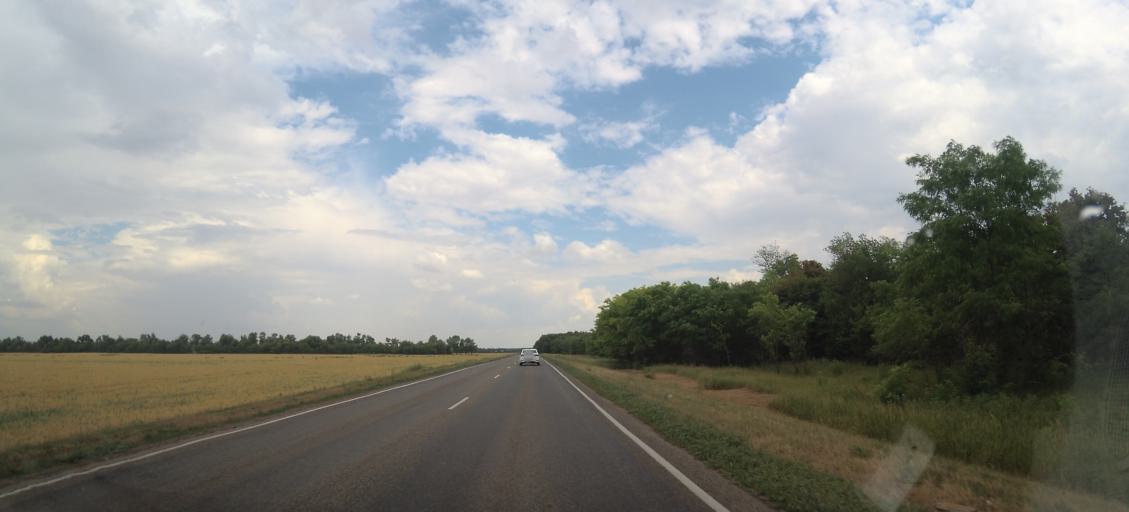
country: RU
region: Rostov
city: Peschanokopskoye
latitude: 46.2037
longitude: 41.2334
